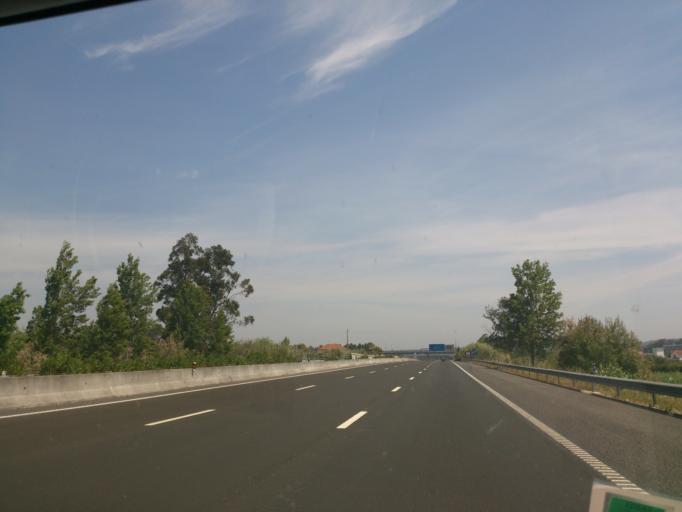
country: PT
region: Leiria
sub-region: Alcobaca
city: Alcobaca
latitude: 39.5827
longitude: -9.0182
